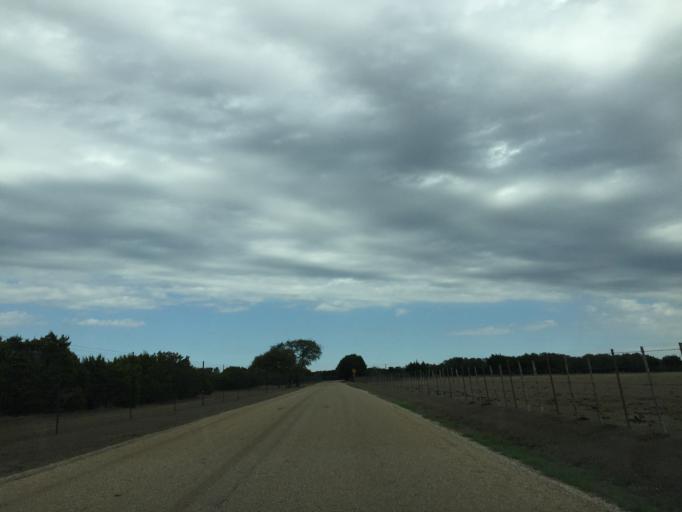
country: US
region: Texas
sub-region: Burnet County
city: Bertram
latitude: 30.6500
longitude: -98.0147
